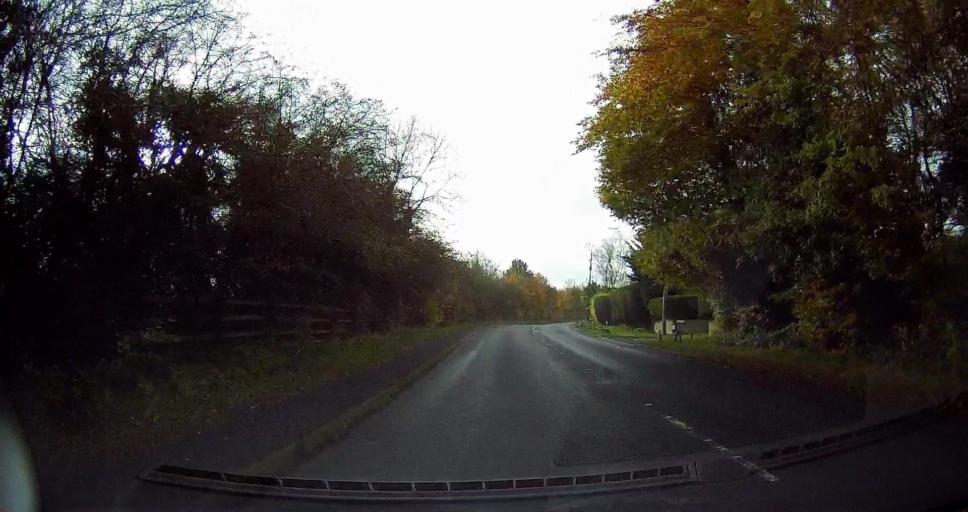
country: GB
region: England
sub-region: Kent
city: Meopham
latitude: 51.3337
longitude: 0.3437
